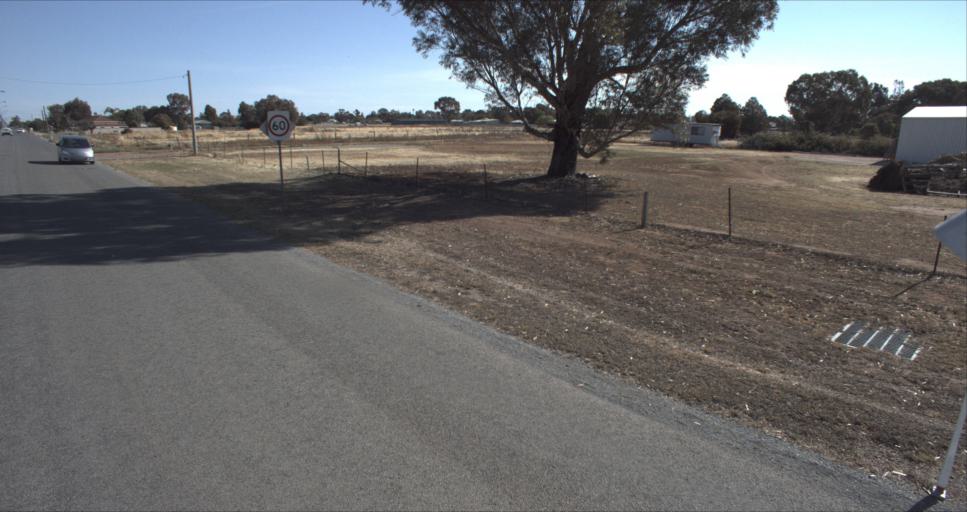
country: AU
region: New South Wales
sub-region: Leeton
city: Leeton
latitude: -34.5446
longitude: 146.4184
